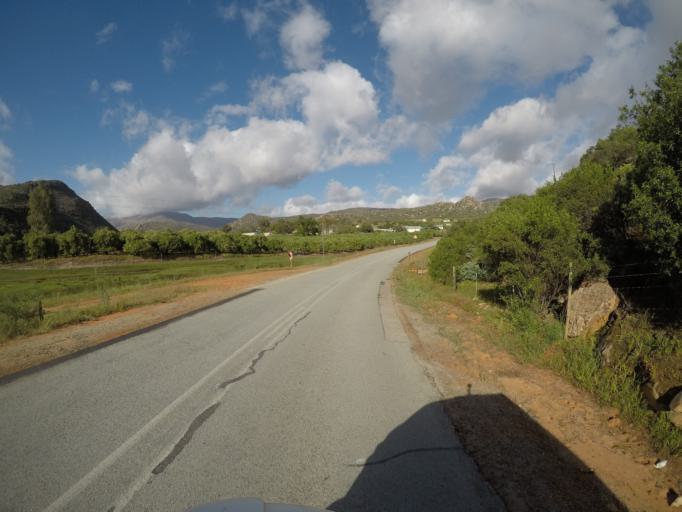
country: ZA
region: Western Cape
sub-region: West Coast District Municipality
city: Clanwilliam
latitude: -32.4374
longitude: 18.9452
